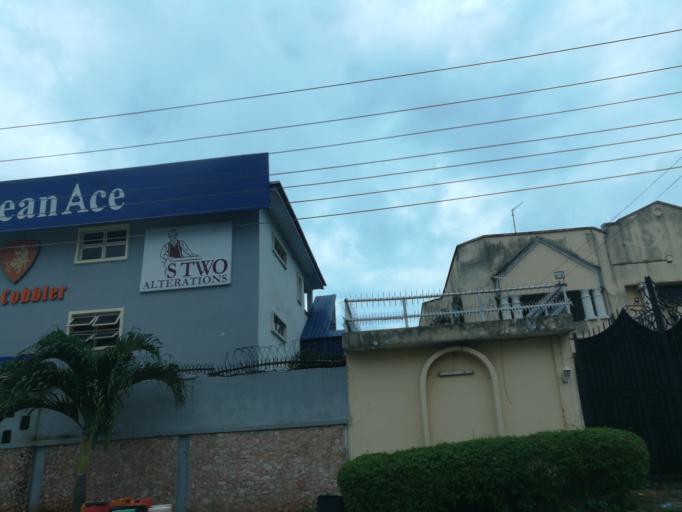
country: NG
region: Lagos
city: Ikoyi
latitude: 6.4484
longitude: 3.4573
